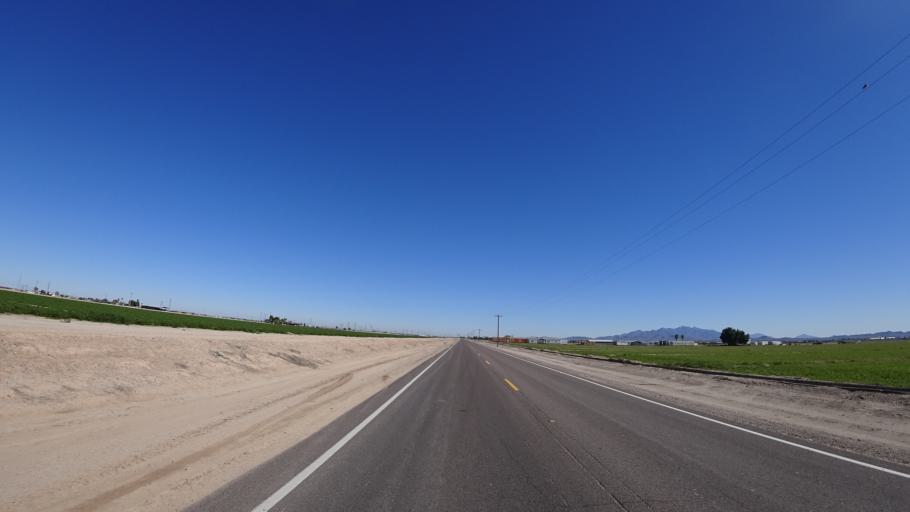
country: US
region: Arizona
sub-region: Maricopa County
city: Buckeye
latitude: 33.4068
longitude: -112.5293
